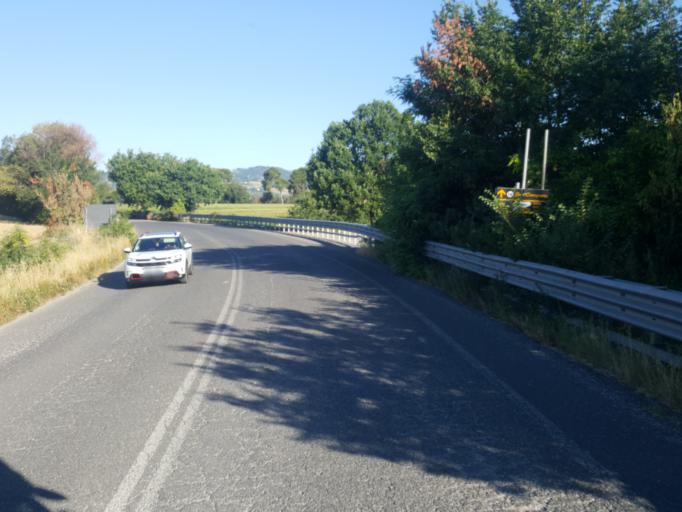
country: IT
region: The Marches
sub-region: Provincia di Pesaro e Urbino
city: Cappone
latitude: 43.8387
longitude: 12.7436
